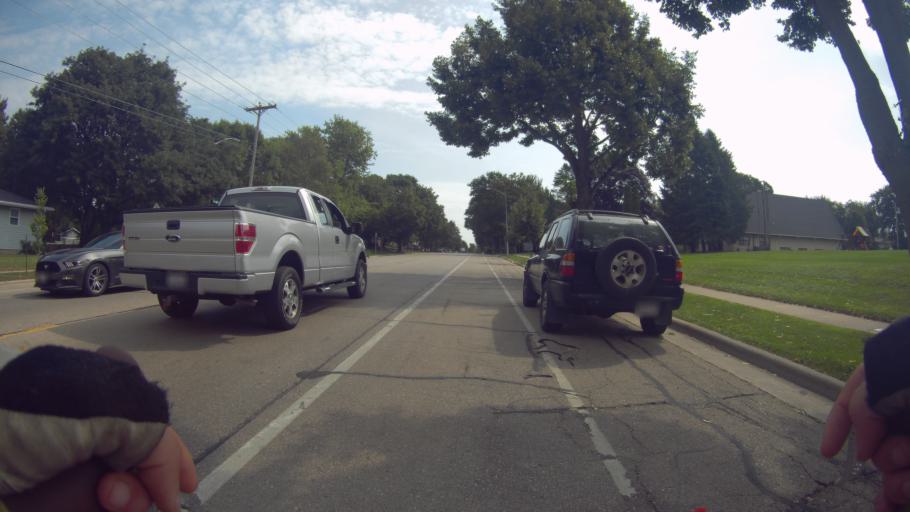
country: US
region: Wisconsin
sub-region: Dane County
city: Monona
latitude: 43.0989
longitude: -89.2976
